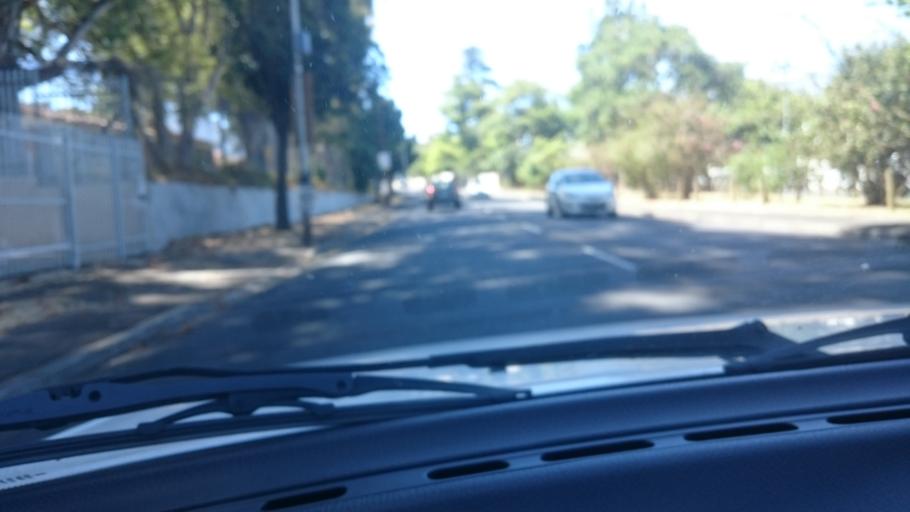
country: ZA
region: Western Cape
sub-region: City of Cape Town
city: Claremont
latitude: -34.0062
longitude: 18.4620
